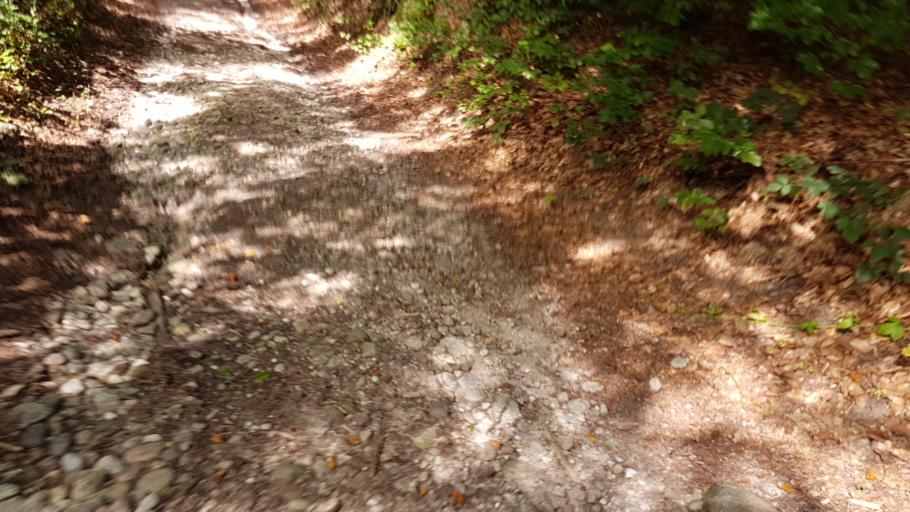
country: CH
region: Lucerne
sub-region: Entlebuch District
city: Oberdiessbach
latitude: 46.8303
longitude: 7.6286
